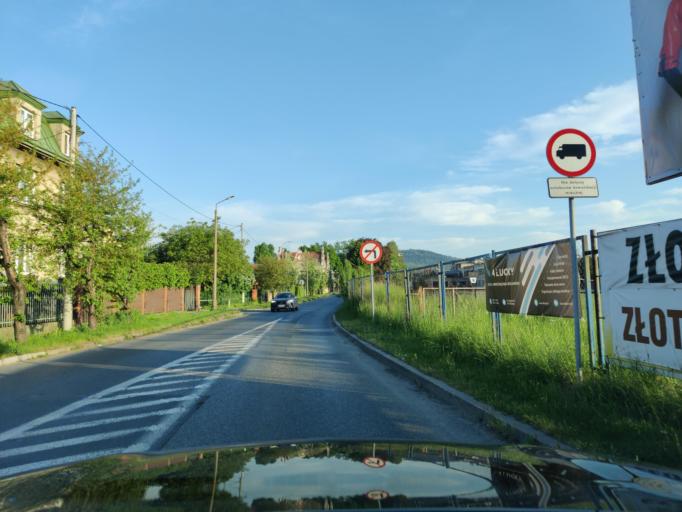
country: PL
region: Silesian Voivodeship
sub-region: Powiat zywiecki
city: Zywiec
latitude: 49.6915
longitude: 19.1939
